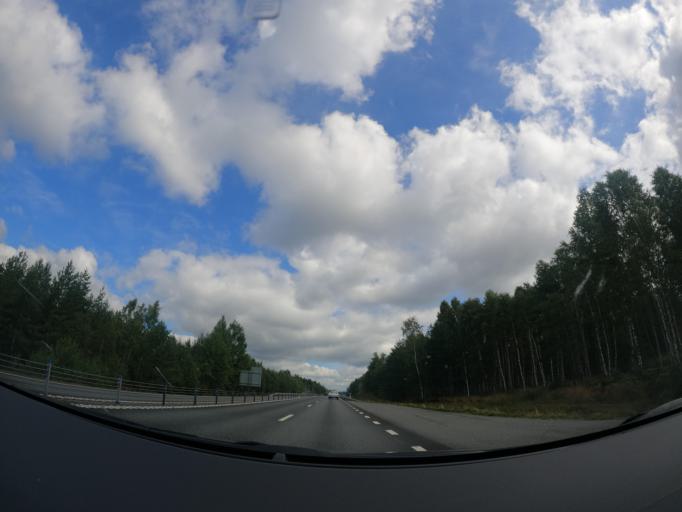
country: SE
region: Joenkoeping
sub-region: Gislaveds Kommun
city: Gislaved
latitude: 57.2977
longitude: 13.5177
